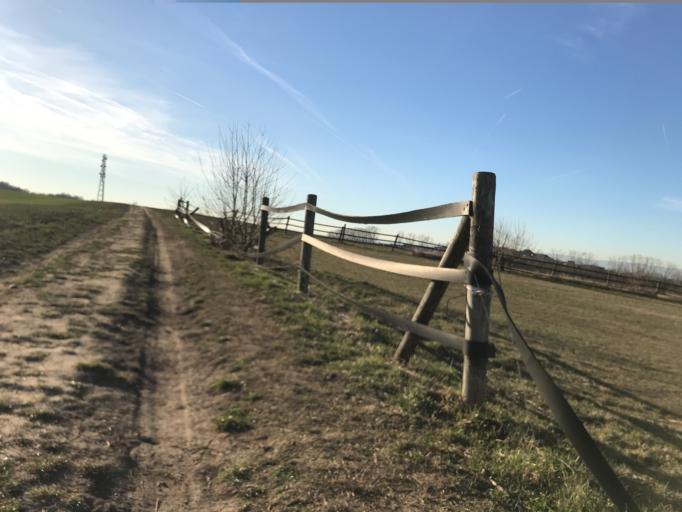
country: DE
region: Rheinland-Pfalz
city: Mainz
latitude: 49.9625
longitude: 8.3004
